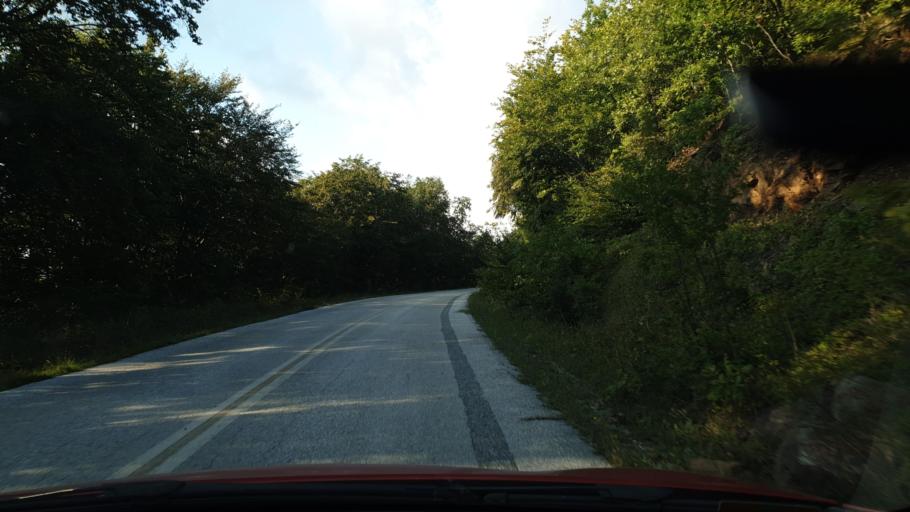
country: GR
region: Central Macedonia
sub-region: Nomos Chalkidikis
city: Galatista
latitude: 40.5082
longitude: 23.2498
